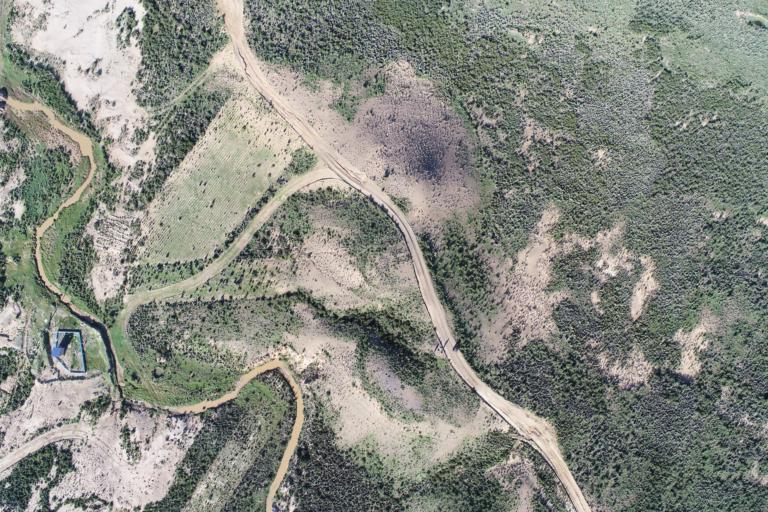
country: BO
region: La Paz
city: Curahuara de Carangas
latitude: -17.2999
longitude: -68.5184
